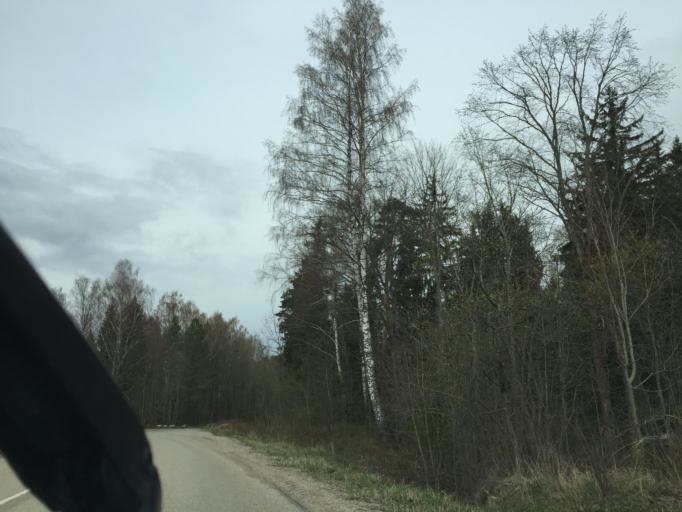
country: LV
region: Amatas Novads
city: Drabesi
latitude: 57.2597
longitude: 25.2721
